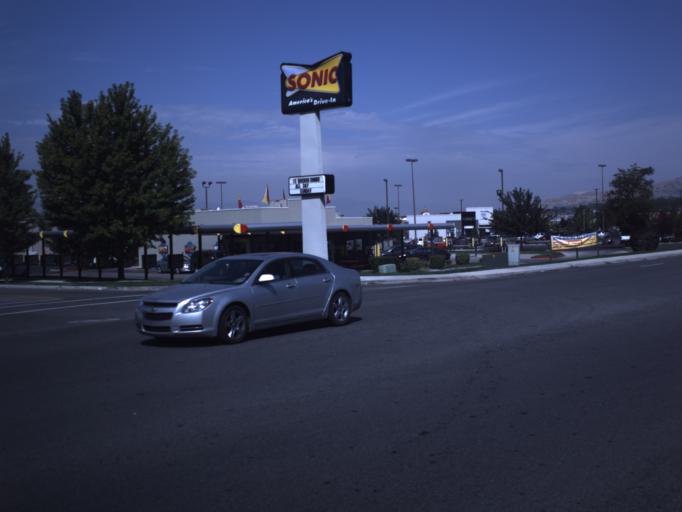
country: US
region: Utah
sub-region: Utah County
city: American Fork
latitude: 40.3795
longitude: -111.8132
